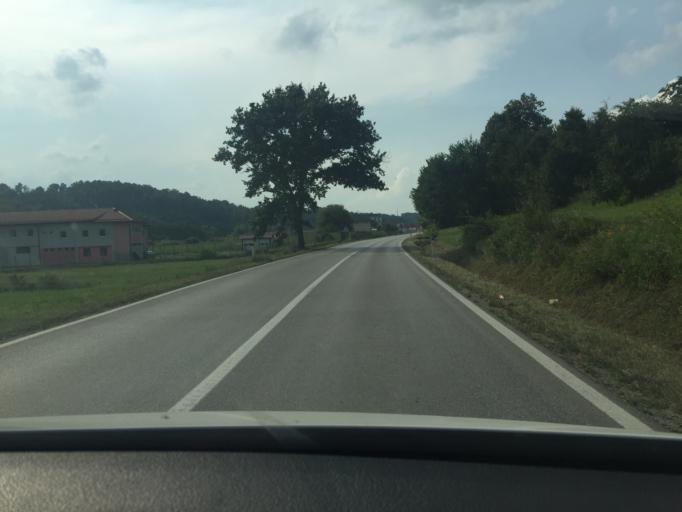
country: BA
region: Federation of Bosnia and Herzegovina
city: Mionica
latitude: 44.8216
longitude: 18.4592
